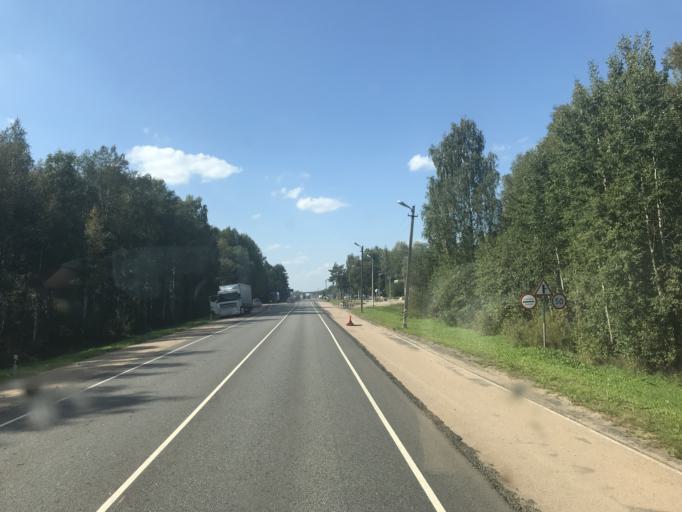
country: RU
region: Smolensk
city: Rudnya
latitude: 54.9855
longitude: 30.9632
